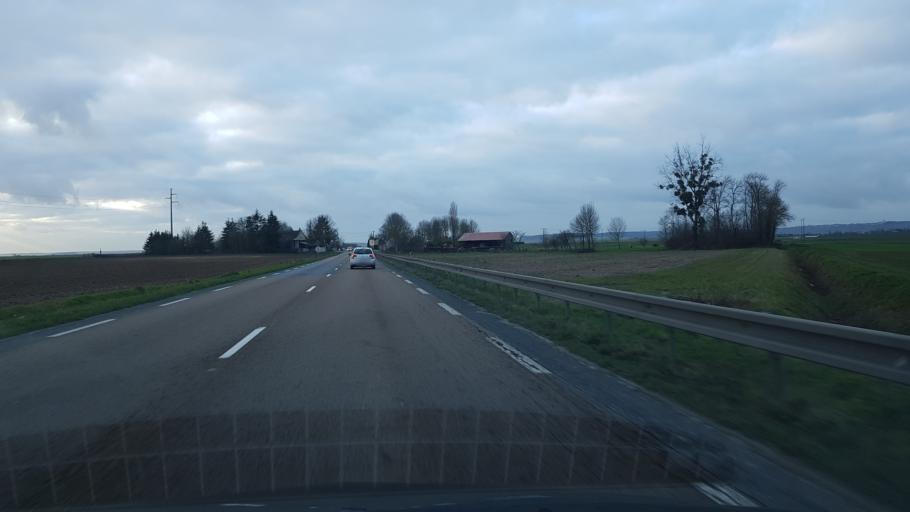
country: FR
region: Champagne-Ardenne
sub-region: Departement de la Marne
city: Connantre
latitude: 48.7257
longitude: 3.8447
